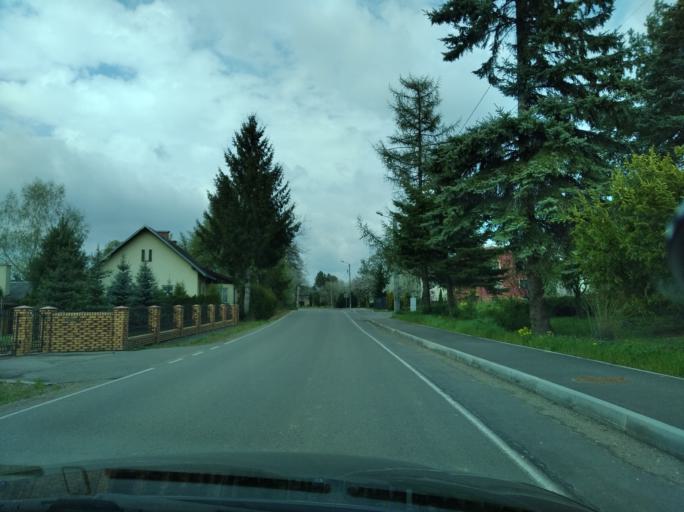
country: PL
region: Subcarpathian Voivodeship
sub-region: Powiat brzozowski
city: Haczow
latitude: 49.6557
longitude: 21.9099
